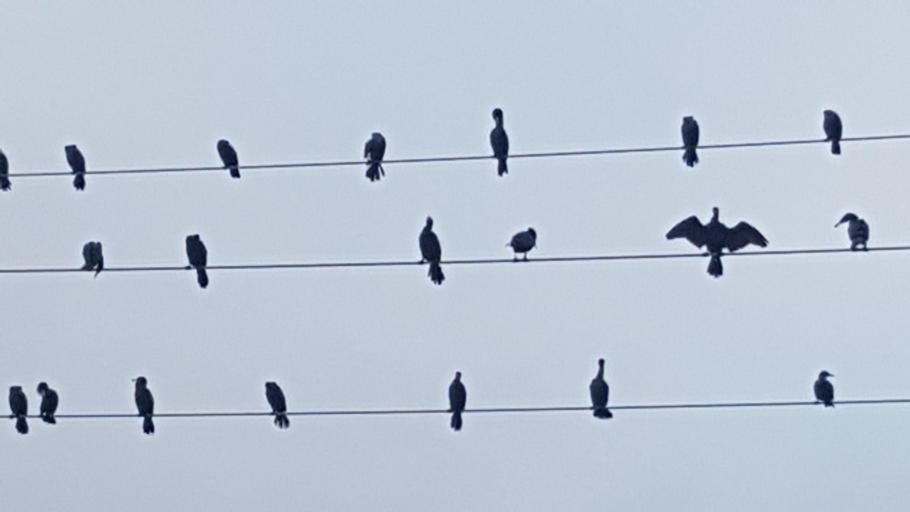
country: PE
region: Lima
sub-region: Lima
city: Pucusana
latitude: -12.4797
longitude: -76.7997
